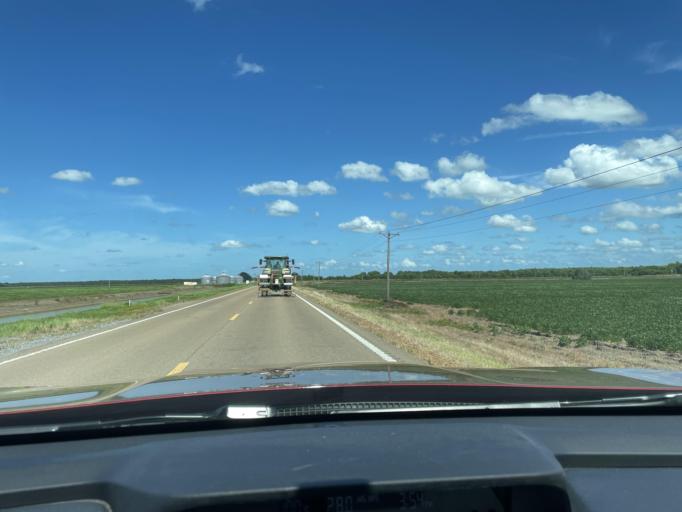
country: US
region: Mississippi
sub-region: Humphreys County
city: Belzoni
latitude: 33.1830
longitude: -90.6546
